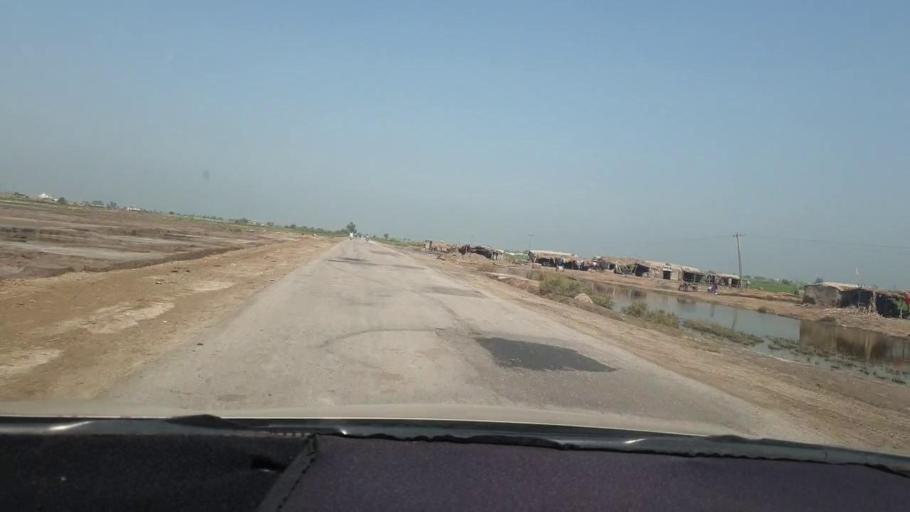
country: PK
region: Sindh
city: Shahdadkot
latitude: 27.8348
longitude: 68.0118
